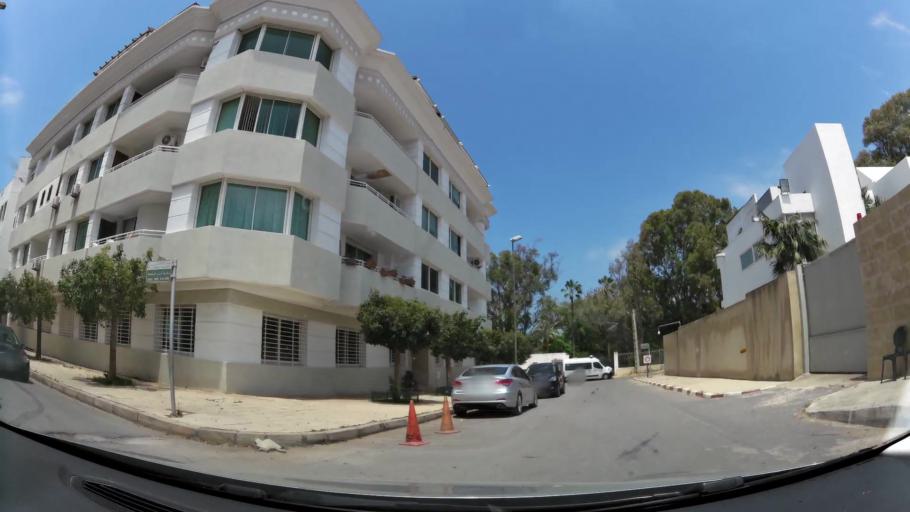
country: MA
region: Rabat-Sale-Zemmour-Zaer
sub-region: Rabat
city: Rabat
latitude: 34.0073
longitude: -6.8474
